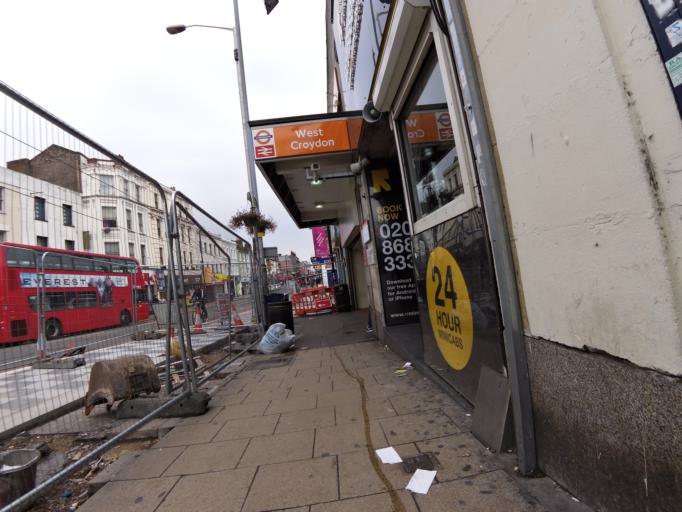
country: GB
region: England
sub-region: Greater London
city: Croydon
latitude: 51.3782
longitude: -0.1028
